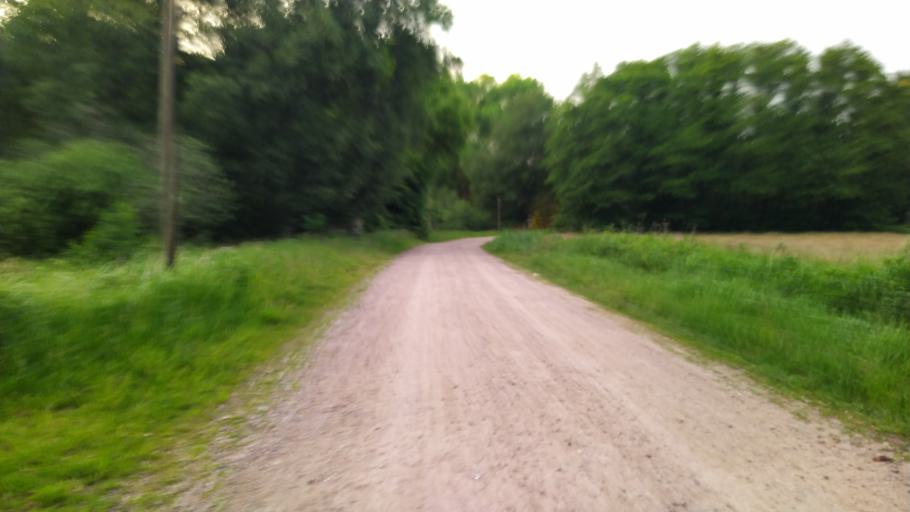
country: DE
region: Lower Saxony
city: Neu Wulmstorf
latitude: 53.4813
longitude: 9.8278
